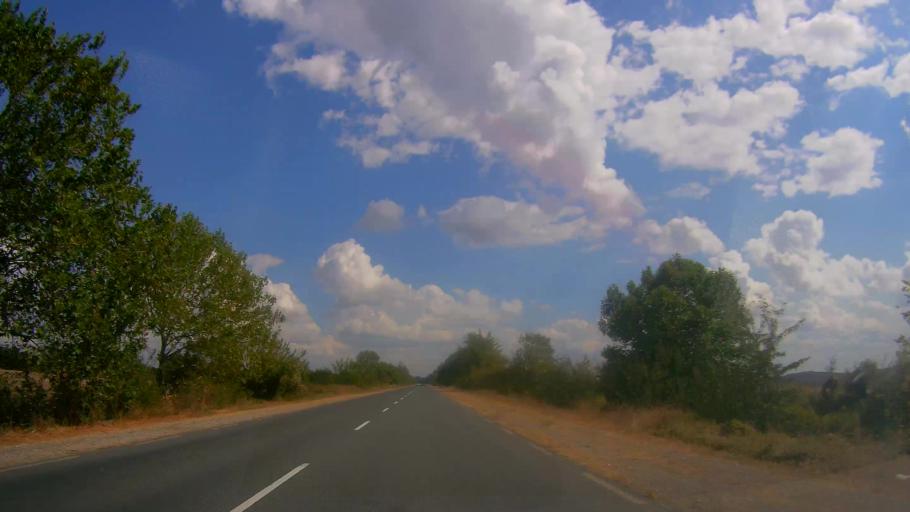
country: BG
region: Sliven
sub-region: Obshtina Sliven
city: Kermen
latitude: 42.6336
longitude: 26.1659
